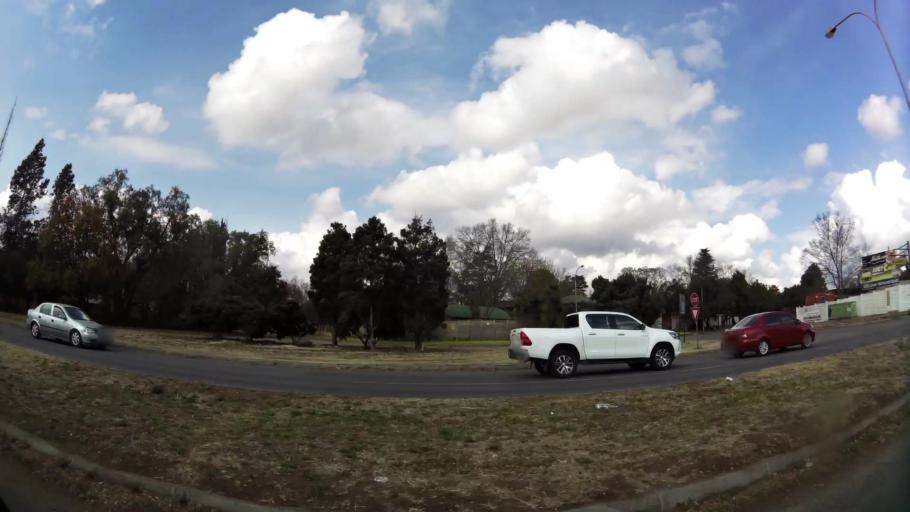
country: ZA
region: Gauteng
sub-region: Sedibeng District Municipality
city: Vanderbijlpark
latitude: -26.7322
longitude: 27.8315
